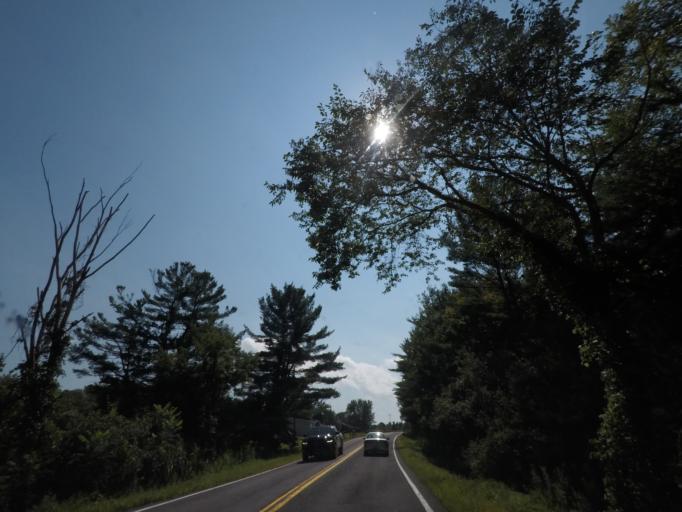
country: US
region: New York
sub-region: Rensselaer County
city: Poestenkill
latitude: 42.8176
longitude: -73.4975
